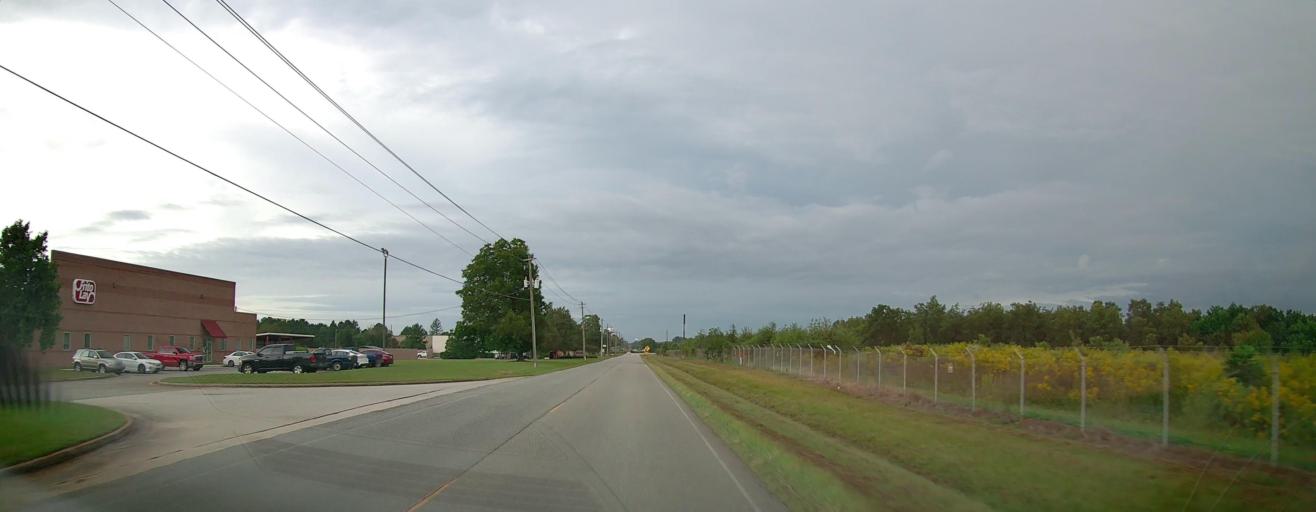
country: US
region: Georgia
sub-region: Peach County
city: Byron
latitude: 32.6515
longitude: -83.7386
